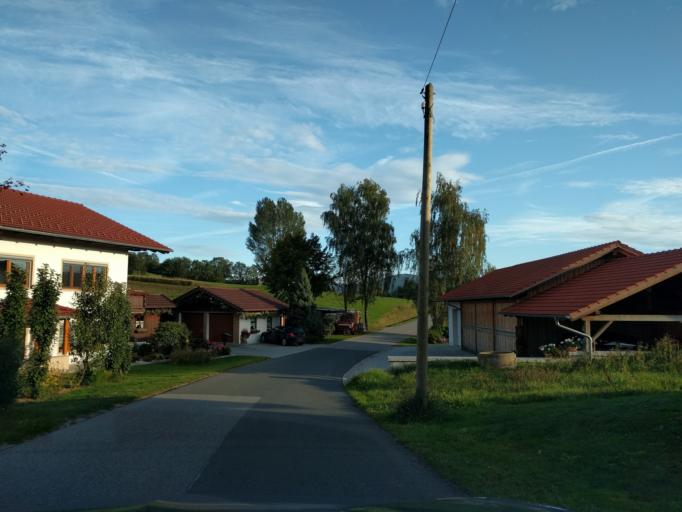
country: DE
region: Bavaria
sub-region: Upper Palatinate
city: Grafenwiesen
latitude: 49.1786
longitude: 12.8857
